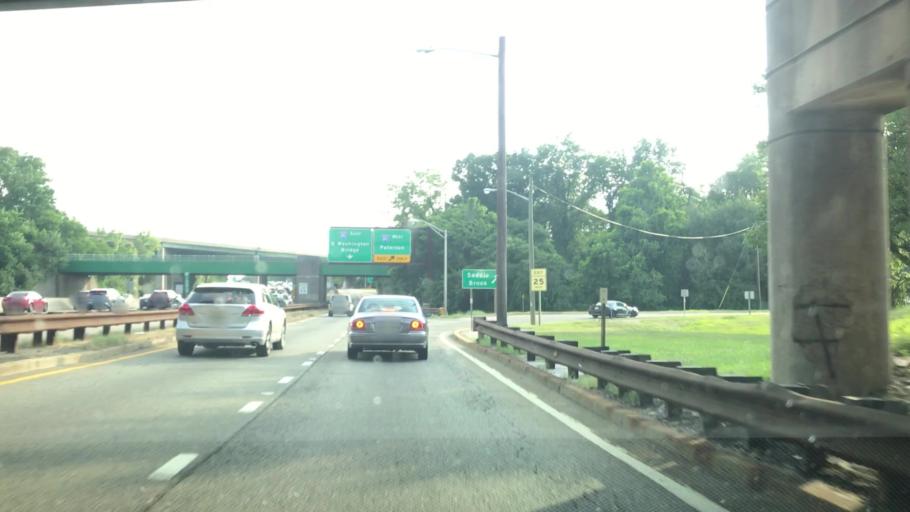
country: US
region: New Jersey
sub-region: Bergen County
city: Elmwood Park
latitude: 40.9057
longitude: -74.1062
